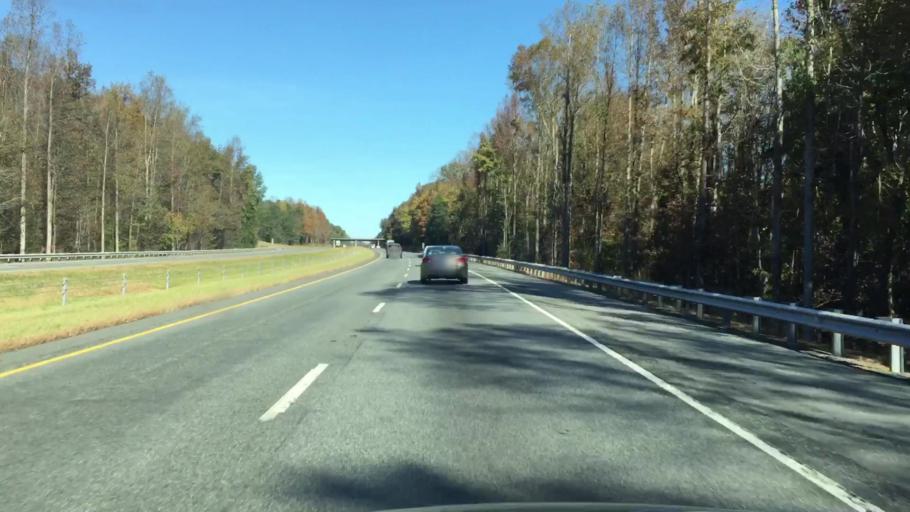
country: US
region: North Carolina
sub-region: Rockingham County
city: Reidsville
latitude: 36.2801
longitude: -79.6399
